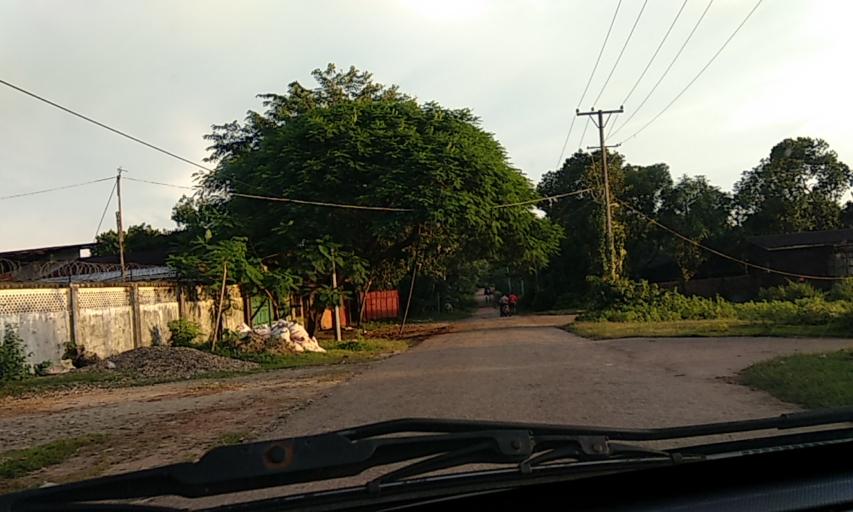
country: MM
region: Mon
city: Mawlamyine
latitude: 16.4577
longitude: 97.6503
